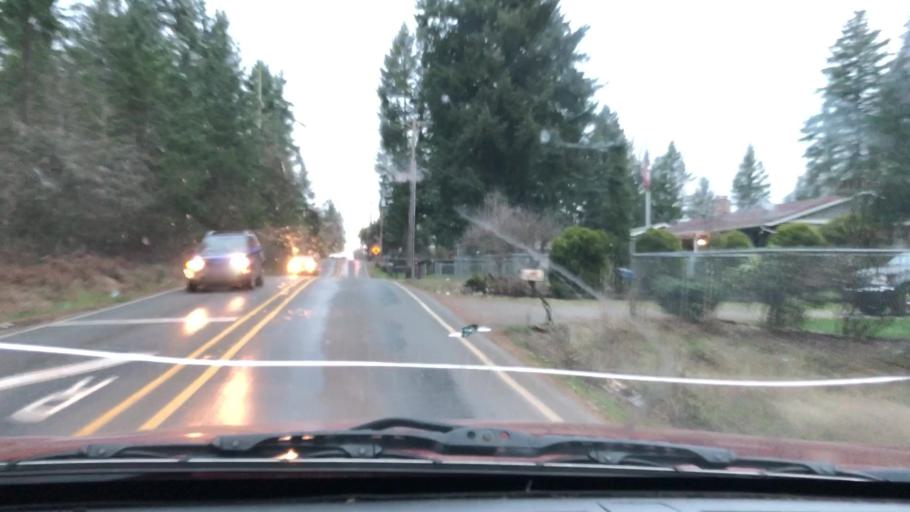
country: US
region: Washington
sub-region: Pierce County
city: Elk Plain
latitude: 47.0661
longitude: -122.4003
